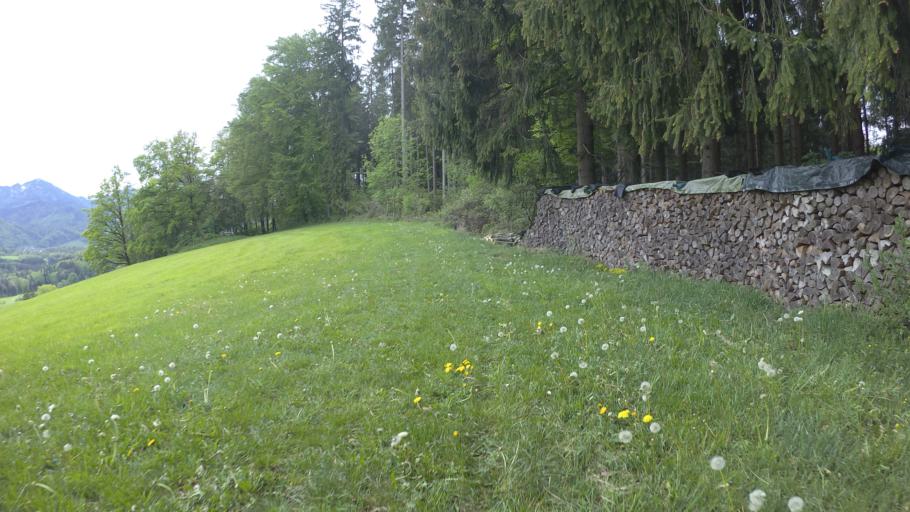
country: DE
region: Bavaria
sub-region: Upper Bavaria
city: Vachendorf
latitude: 47.8309
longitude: 12.6165
